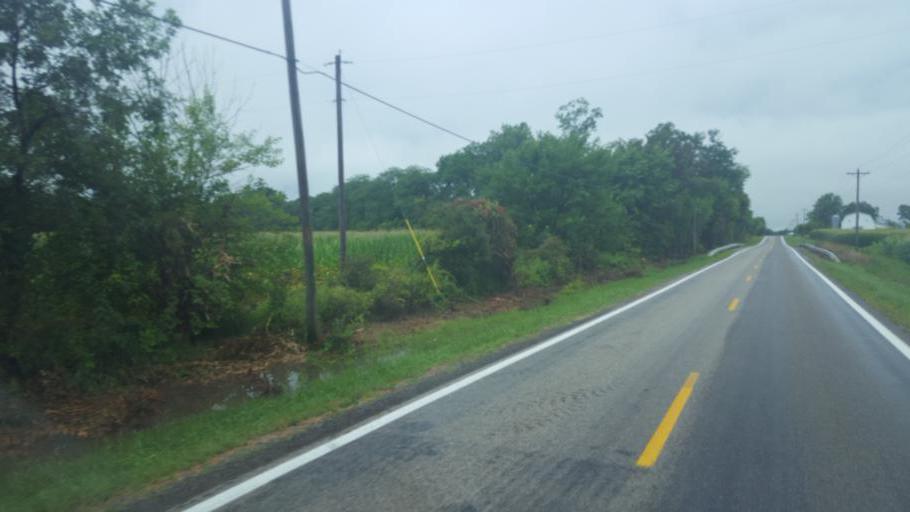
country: US
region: Ohio
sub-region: Union County
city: Richwood
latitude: 40.5453
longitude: -83.3633
